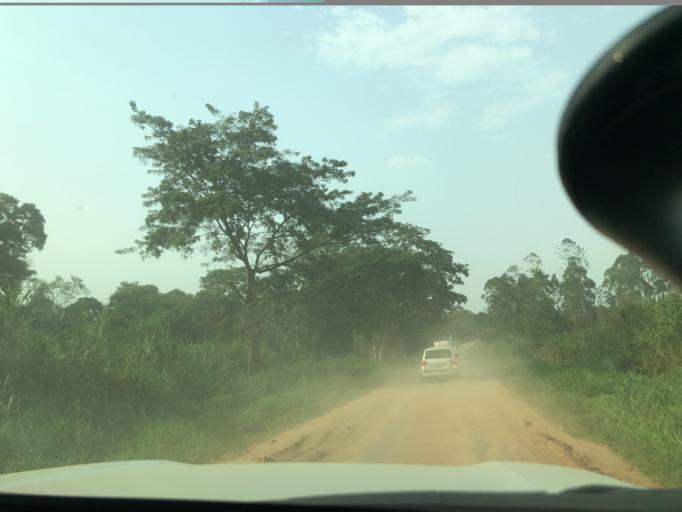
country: UG
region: Western Region
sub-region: Kasese District
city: Margherita
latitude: 0.1908
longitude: 29.6570
